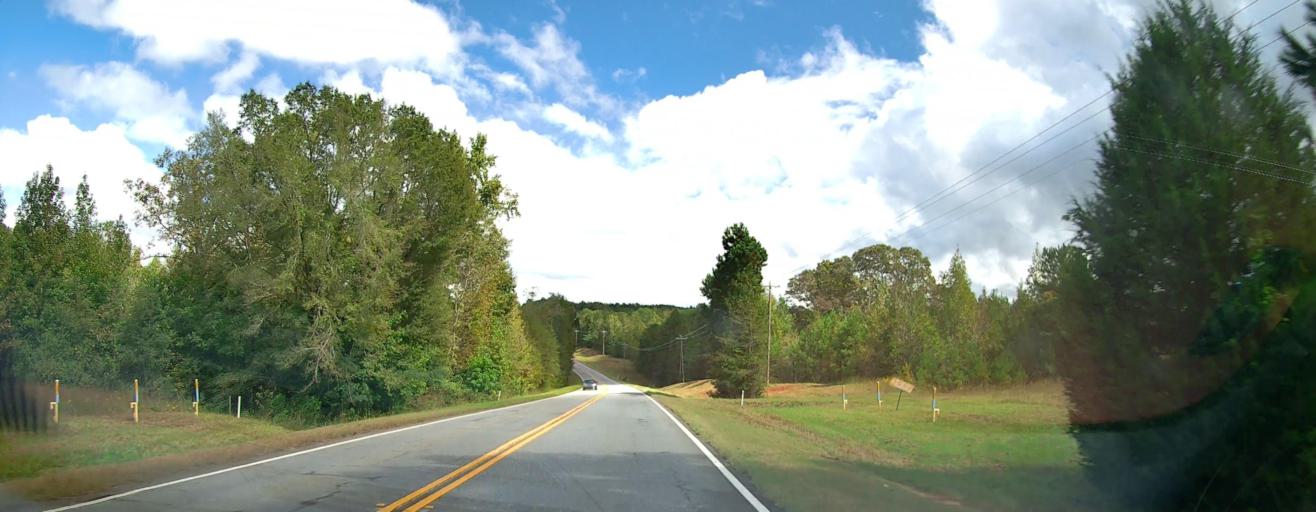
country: US
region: Georgia
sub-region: Jones County
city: Gray
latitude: 32.9852
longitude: -83.4097
